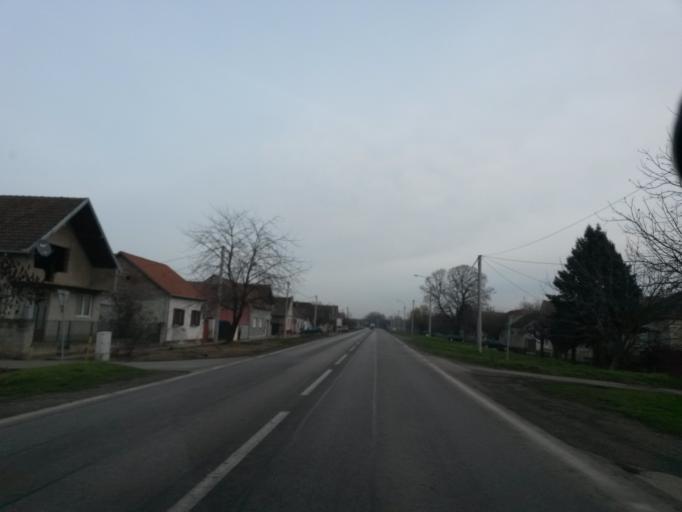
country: HR
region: Vukovarsko-Srijemska
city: Brsadin
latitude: 45.3616
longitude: 18.9104
